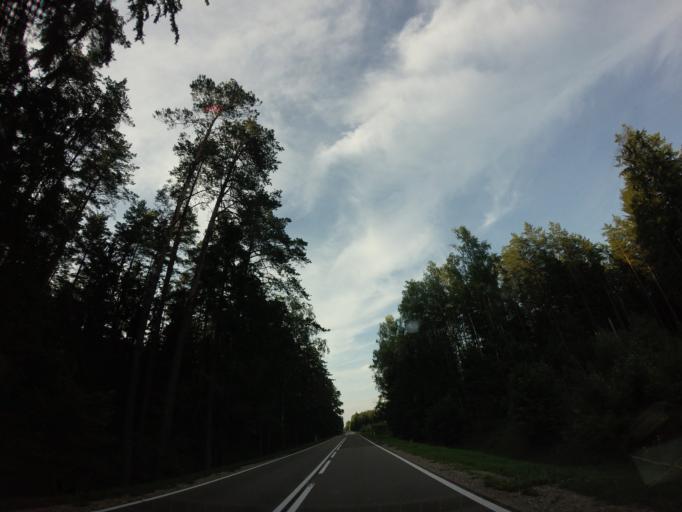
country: PL
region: Podlasie
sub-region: Powiat sejnenski
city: Sejny
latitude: 53.9947
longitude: 23.3089
